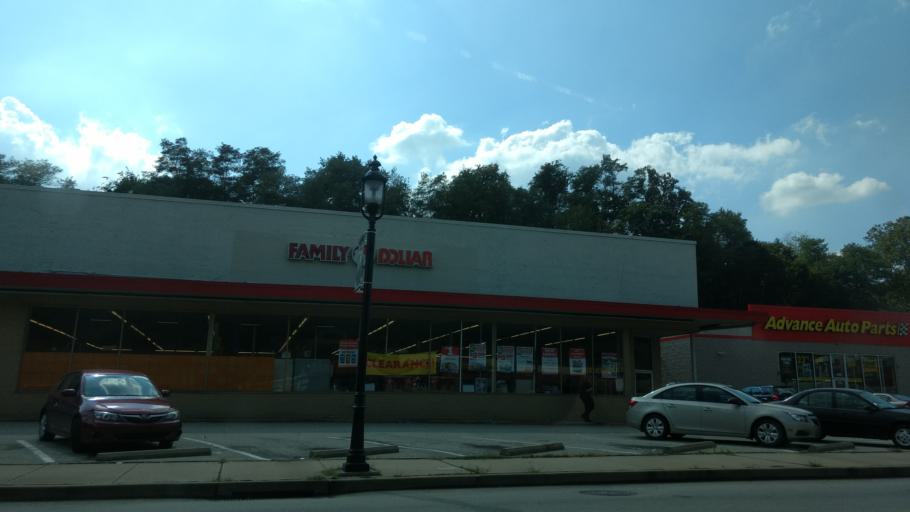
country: US
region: Pennsylvania
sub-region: Washington County
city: New Eagle
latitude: 40.2065
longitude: -79.9383
